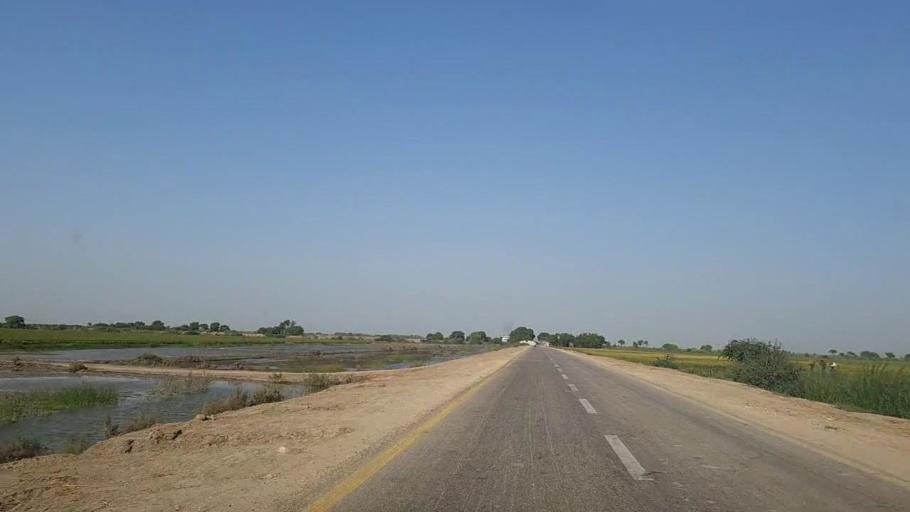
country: PK
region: Sindh
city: Jati
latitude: 24.4124
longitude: 68.3008
